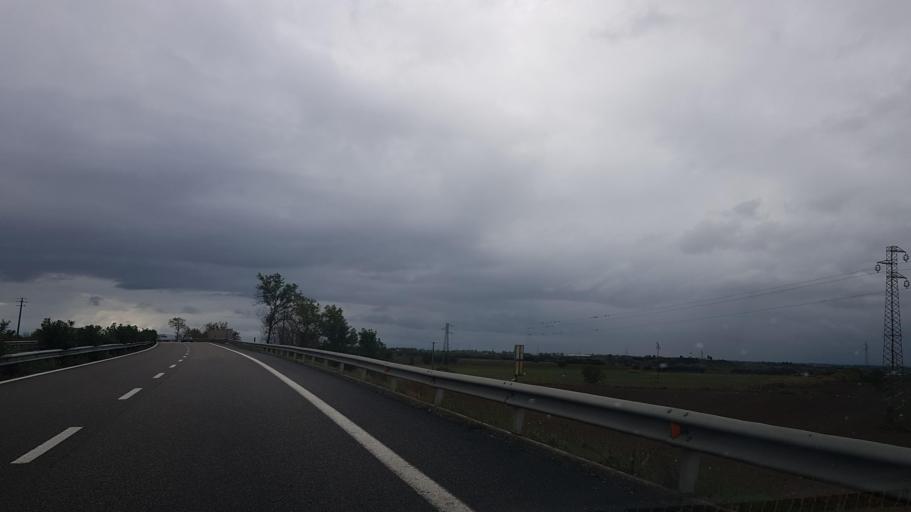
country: IT
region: Apulia
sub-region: Provincia di Taranto
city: Marina di Ginosa
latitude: 40.4306
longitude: 16.8298
